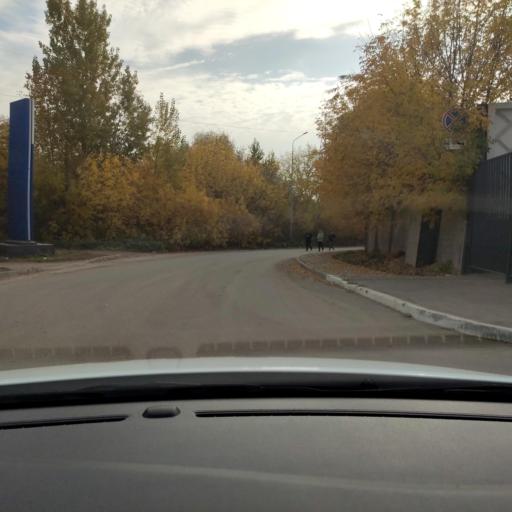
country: RU
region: Tatarstan
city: Verkhniy Uslon
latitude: 55.8037
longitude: 49.0476
